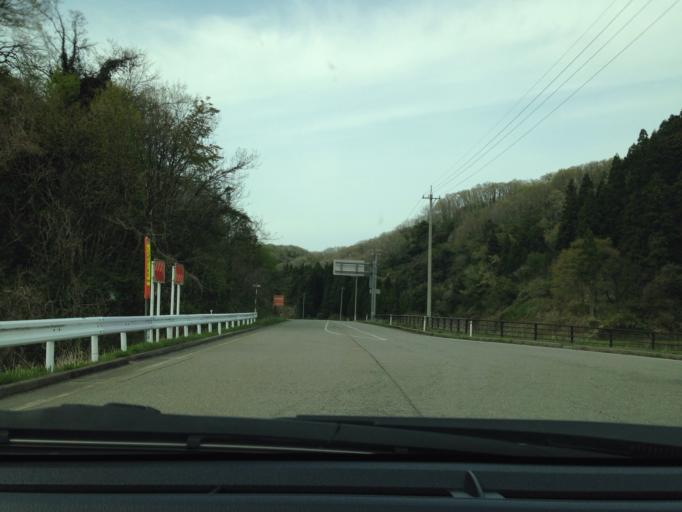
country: JP
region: Ishikawa
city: Kanazawa-shi
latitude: 36.5500
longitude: 136.7310
